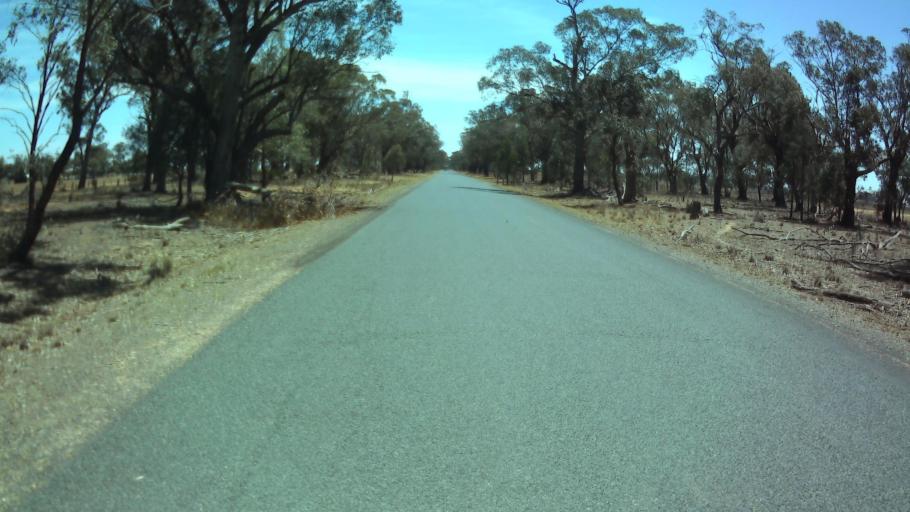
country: AU
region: New South Wales
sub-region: Weddin
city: Grenfell
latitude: -34.0038
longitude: 147.7625
